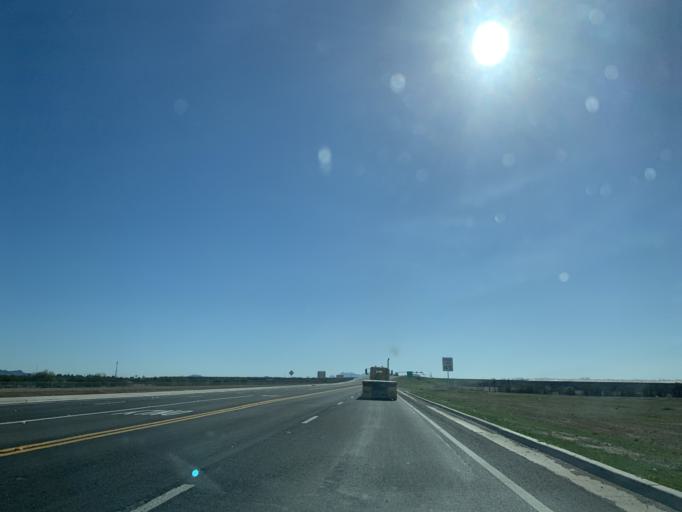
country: US
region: Arizona
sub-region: Pinal County
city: Eloy
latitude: 32.7339
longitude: -111.5160
